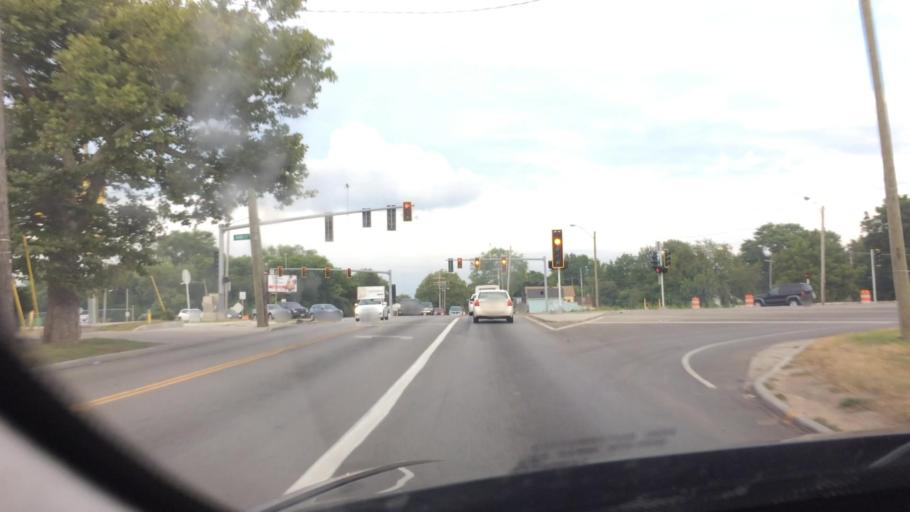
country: US
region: Ohio
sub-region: Wood County
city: Rossford
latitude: 41.6308
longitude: -83.5680
